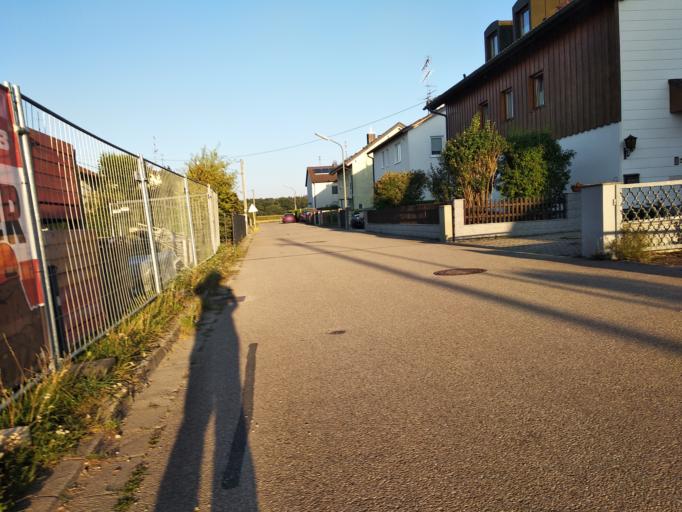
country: DE
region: Bavaria
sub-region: Upper Bavaria
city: Forstinning
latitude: 48.1690
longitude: 11.9183
